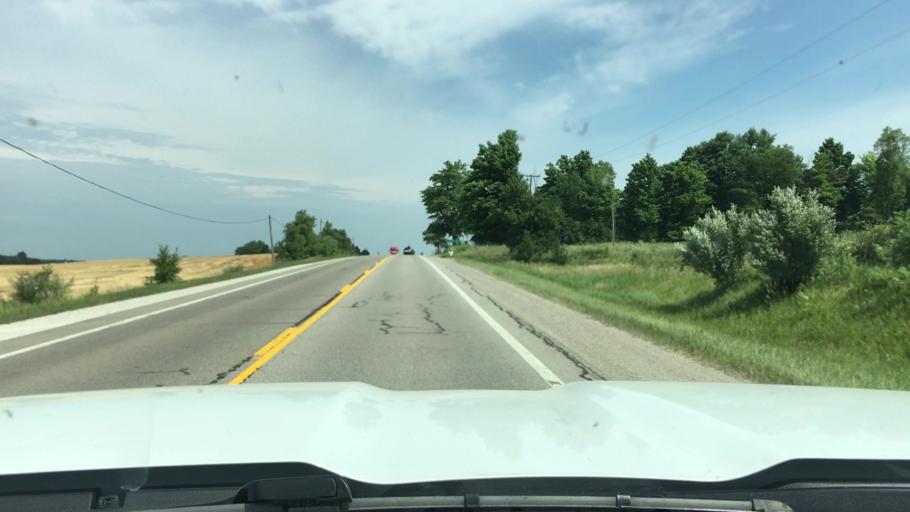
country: US
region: Michigan
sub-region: Sanilac County
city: Brown City
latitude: 43.1857
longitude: -83.0764
